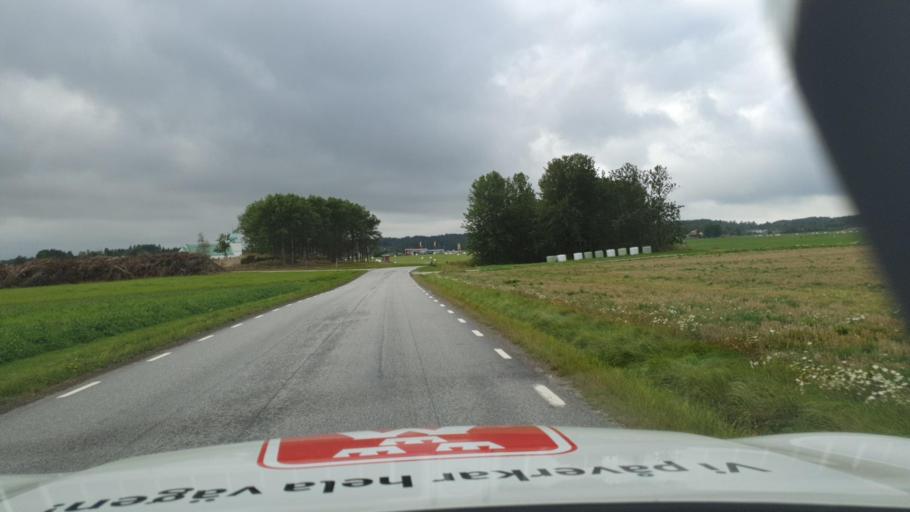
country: SE
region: Vaestra Goetaland
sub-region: Orust
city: Henan
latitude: 58.1563
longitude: 11.5953
